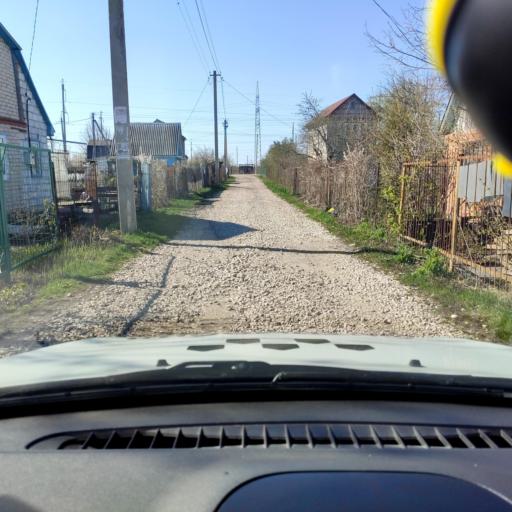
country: RU
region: Samara
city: Tol'yatti
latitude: 53.5926
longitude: 49.2933
